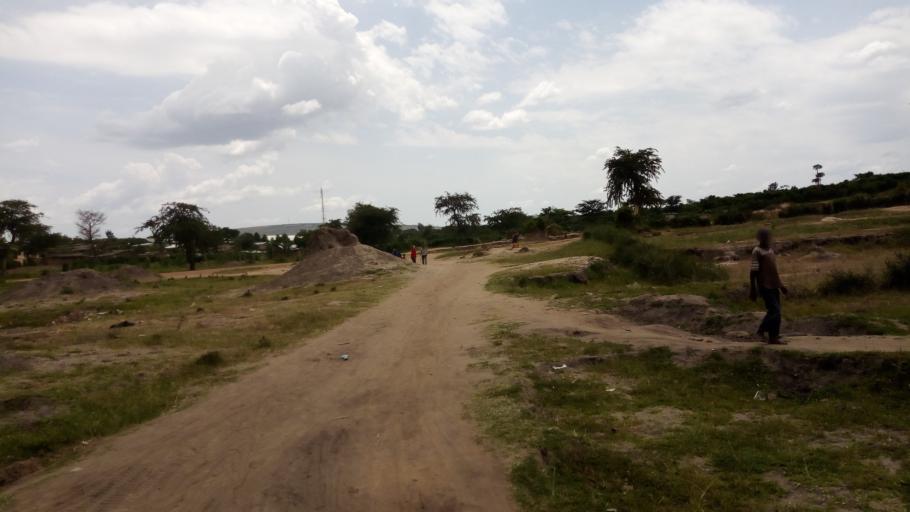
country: UG
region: Western Region
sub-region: Isingiro District
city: Isingiro
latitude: -0.7724
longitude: 30.9454
